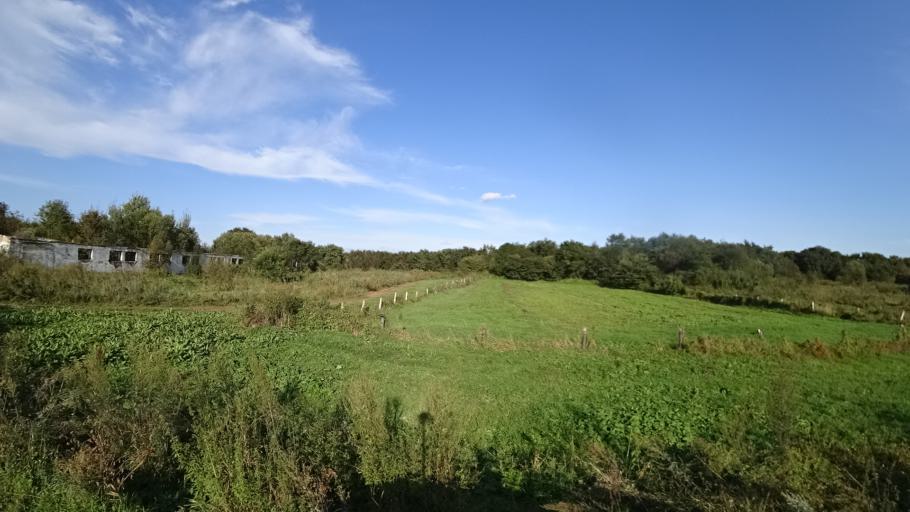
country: RU
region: Amur
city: Arkhara
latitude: 49.3486
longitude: 130.1065
